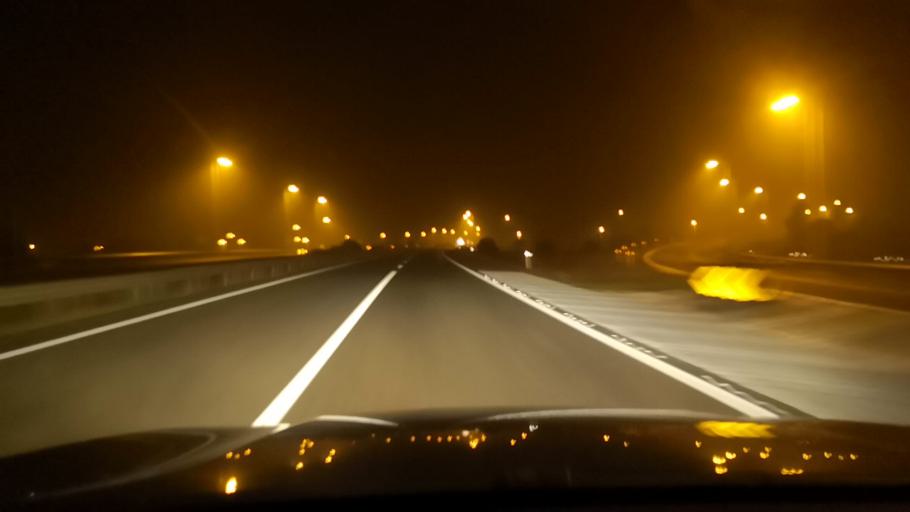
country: PT
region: Santarem
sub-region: Benavente
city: Poceirao
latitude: 38.8392
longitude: -8.7297
